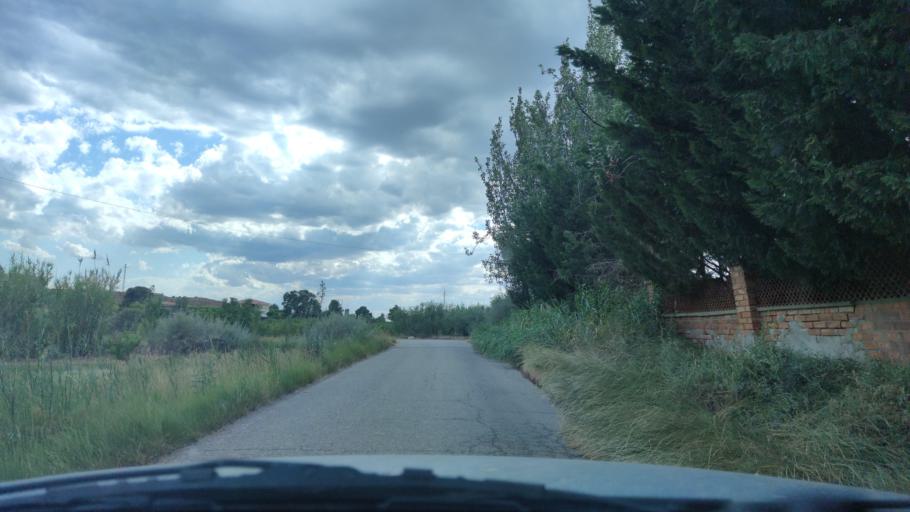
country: ES
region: Catalonia
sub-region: Provincia de Lleida
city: Alpicat
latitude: 41.6288
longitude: 0.5769
